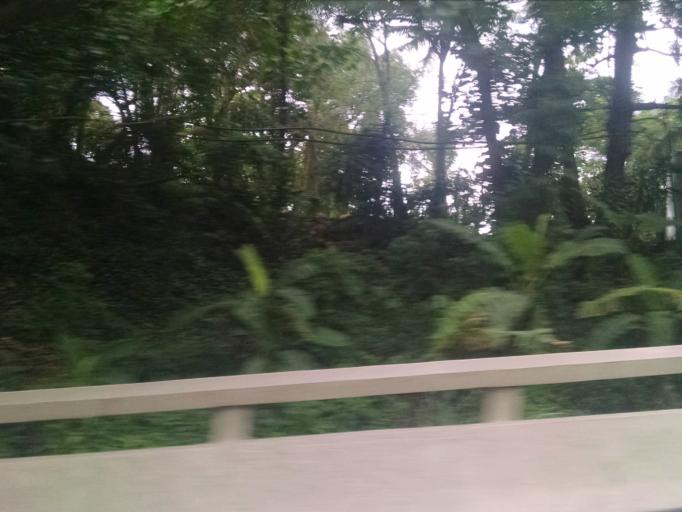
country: BR
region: Rio de Janeiro
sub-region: Rio De Janeiro
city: Rio de Janeiro
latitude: -23.0045
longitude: -43.2780
